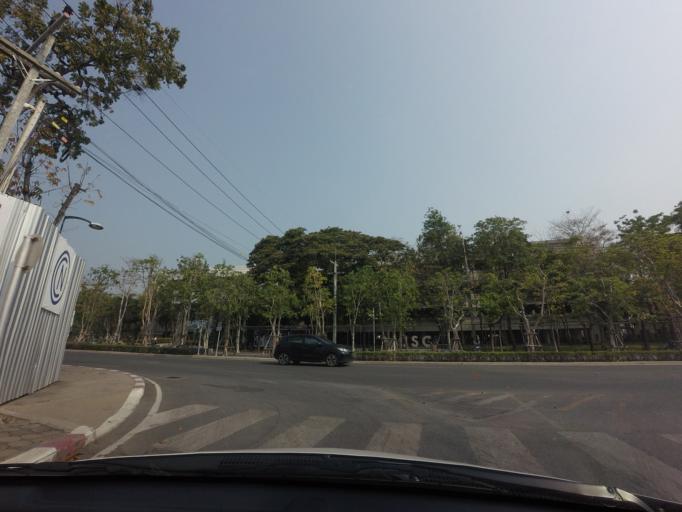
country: TH
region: Nakhon Pathom
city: Salaya
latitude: 13.7918
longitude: 100.3225
